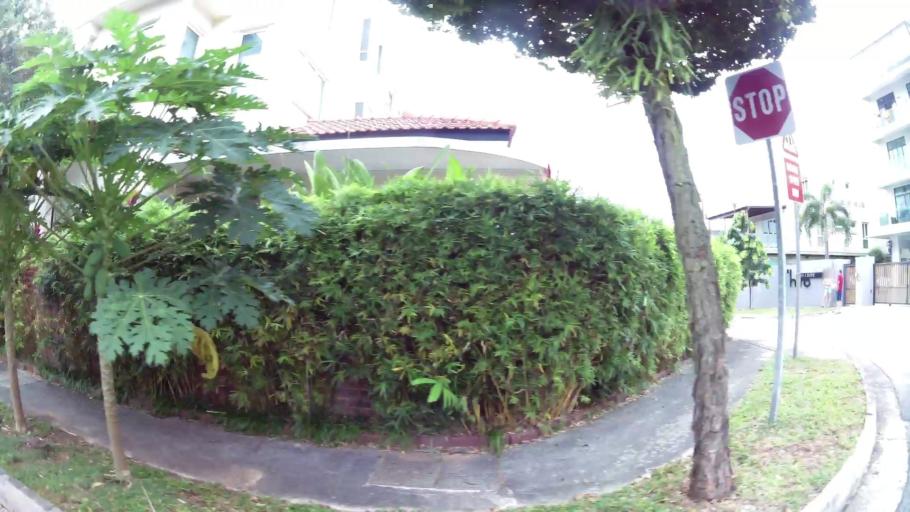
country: SG
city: Singapore
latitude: 1.3603
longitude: 103.8750
